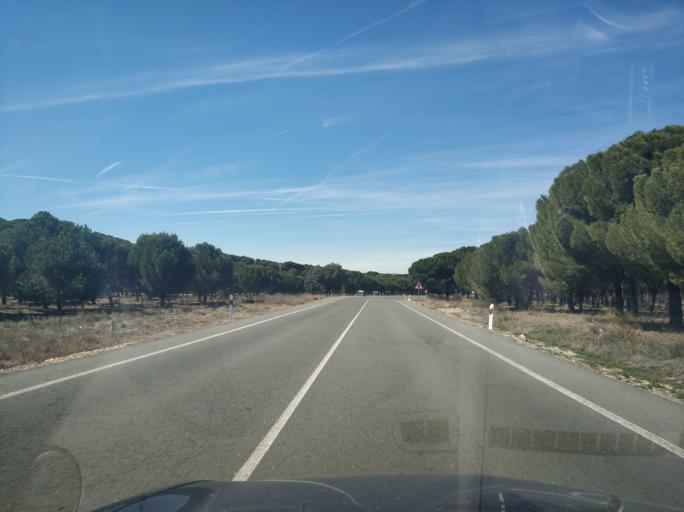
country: ES
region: Castille and Leon
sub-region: Provincia de Valladolid
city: Viana de Cega
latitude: 41.5394
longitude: -4.7716
